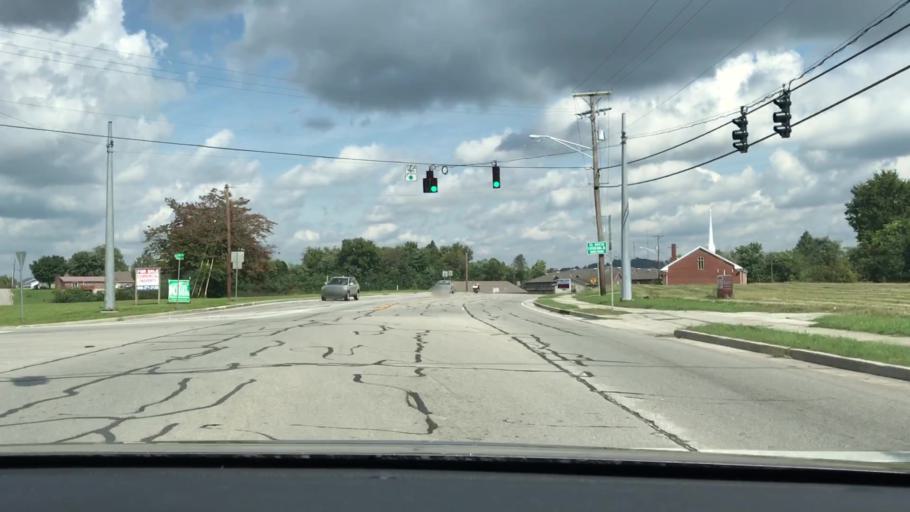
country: US
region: Kentucky
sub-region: Pulaski County
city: Somerset
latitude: 37.0759
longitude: -84.6152
